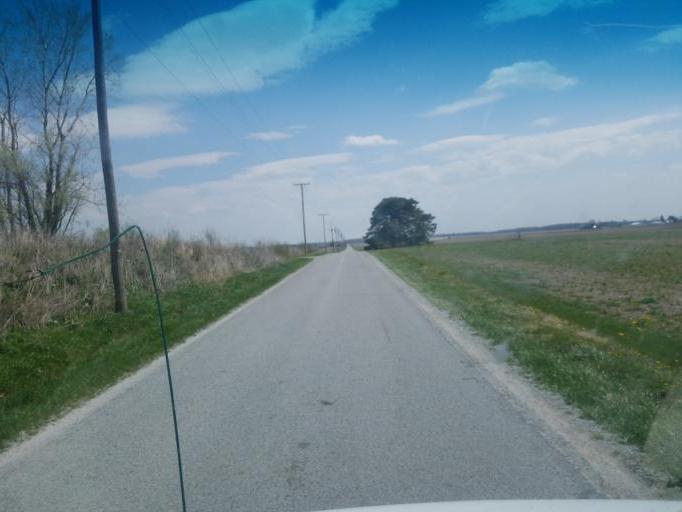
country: US
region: Ohio
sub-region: Hardin County
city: Forest
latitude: 40.7599
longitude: -83.5282
